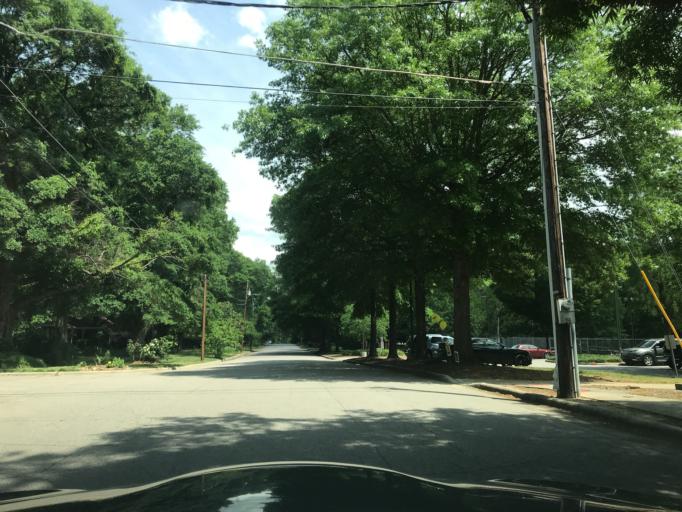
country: US
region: North Carolina
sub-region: Wake County
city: Raleigh
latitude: 35.7762
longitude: -78.6185
